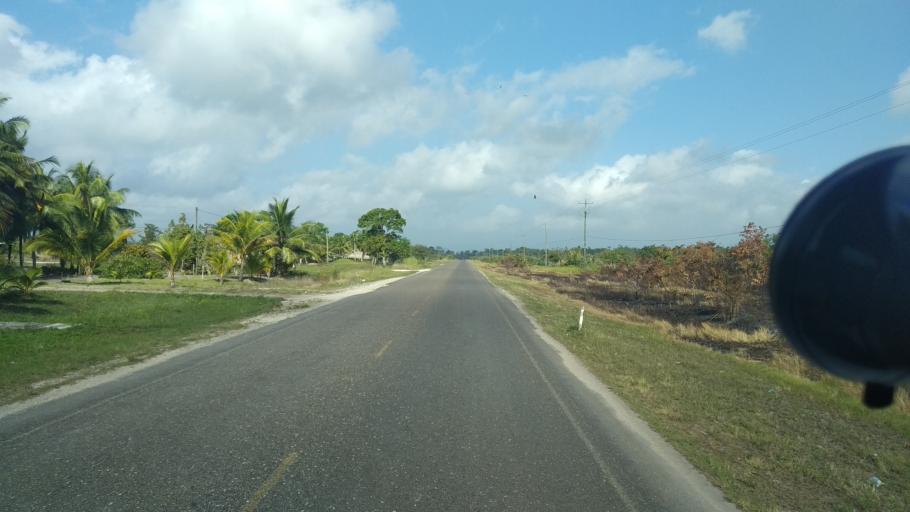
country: BZ
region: Stann Creek
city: Placencia
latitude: 16.5136
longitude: -88.5444
